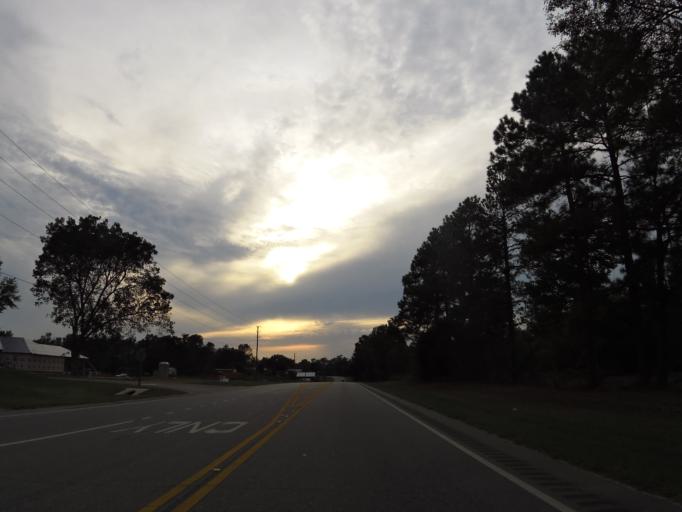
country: US
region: Alabama
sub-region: Escambia County
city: Atmore
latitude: 31.0230
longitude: -87.5238
